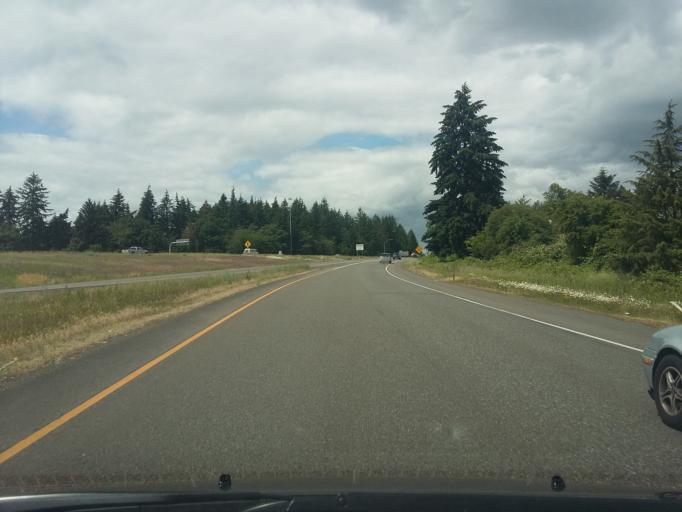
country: US
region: Washington
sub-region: Clark County
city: Orchards
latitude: 45.6076
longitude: -122.5507
